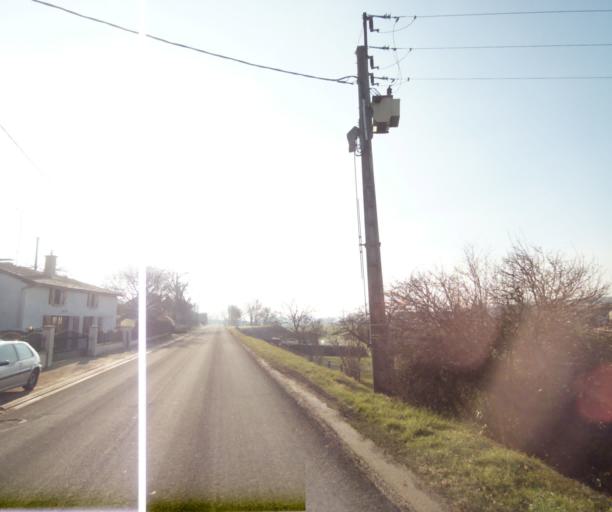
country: FR
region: Champagne-Ardenne
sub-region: Departement de la Haute-Marne
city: Wassy
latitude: 48.4686
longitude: 4.9702
